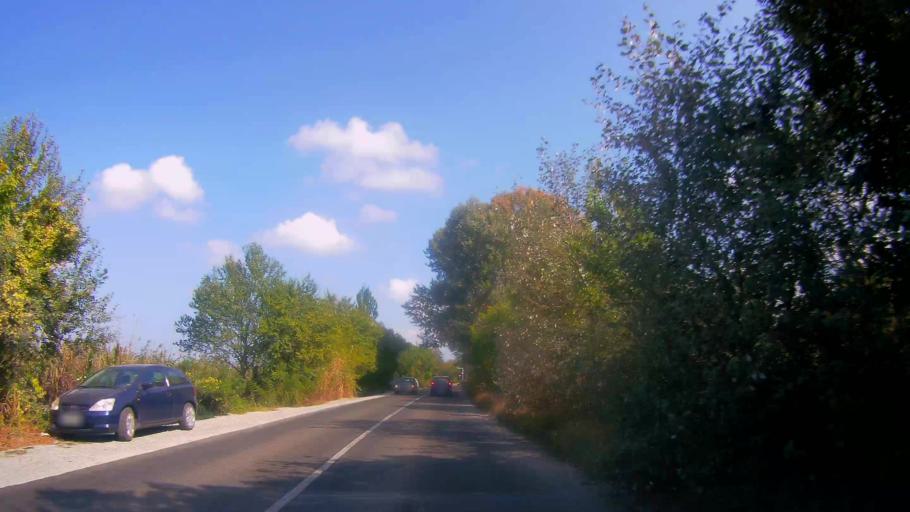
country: BG
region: Burgas
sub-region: Obshtina Burgas
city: Burgas
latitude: 42.4731
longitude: 27.4244
